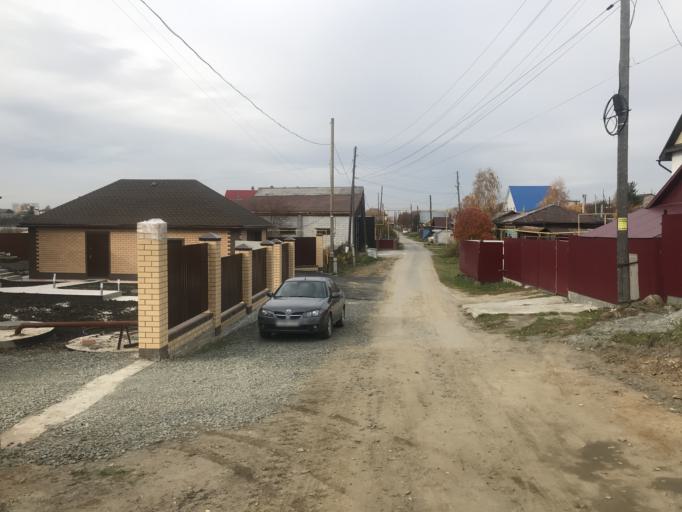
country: RU
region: Sverdlovsk
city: Aramil
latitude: 56.7028
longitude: 60.8345
